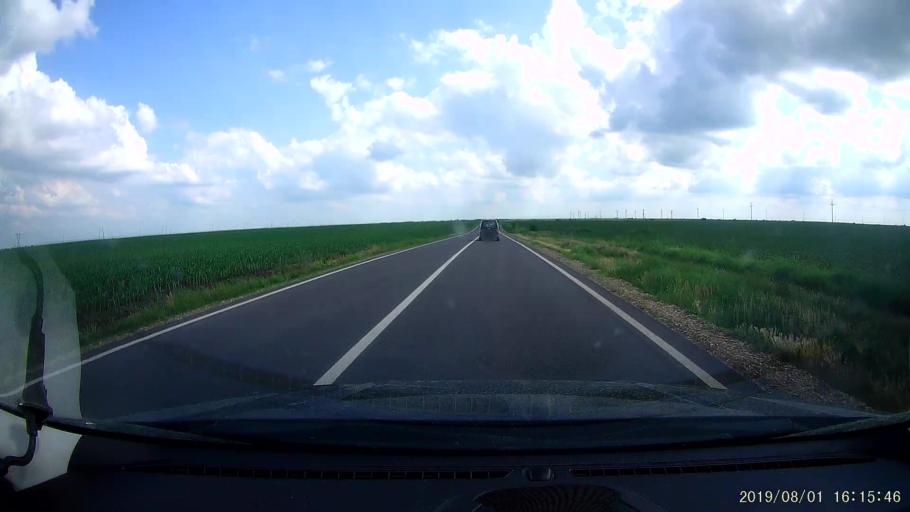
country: RO
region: Calarasi
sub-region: Comuna Stefan Voda
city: Stefan Voda
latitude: 44.3320
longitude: 27.3600
